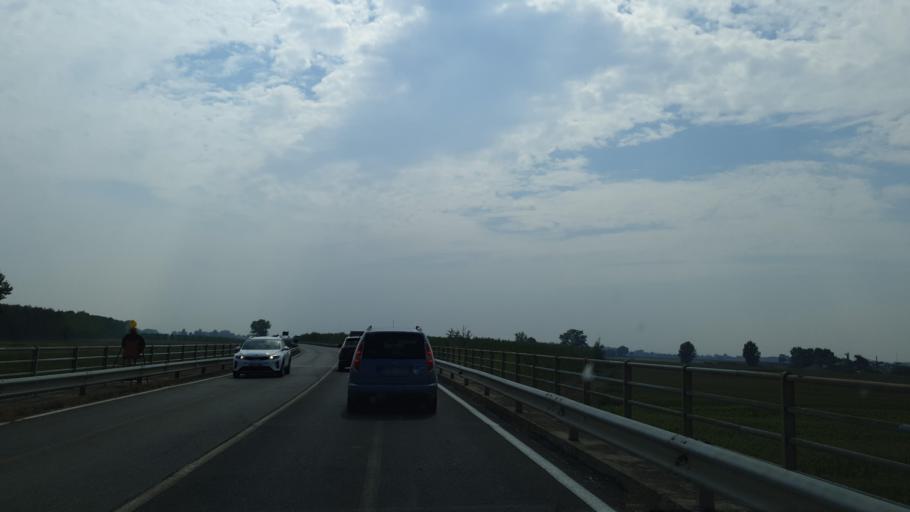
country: IT
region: Lombardy
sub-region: Provincia di Cremona
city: San Daniele Po
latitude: 45.0356
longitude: 10.1770
